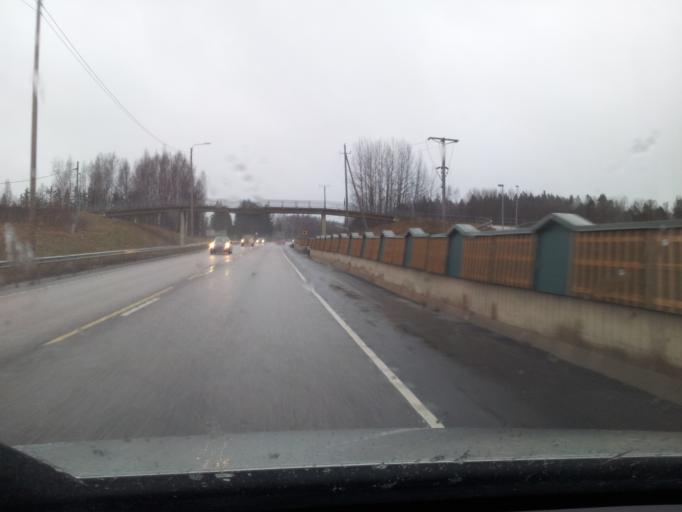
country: FI
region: Uusimaa
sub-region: Helsinki
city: Kirkkonummi
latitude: 60.1545
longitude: 24.5421
